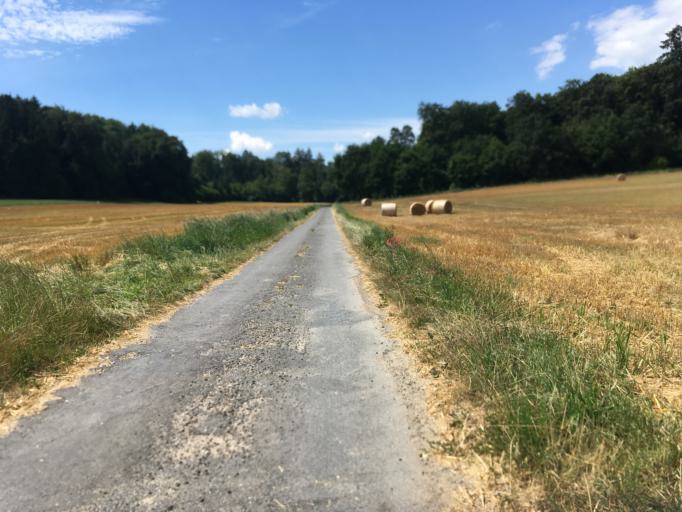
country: CH
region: Fribourg
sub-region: Broye District
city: Domdidier
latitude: 46.9367
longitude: 6.9956
